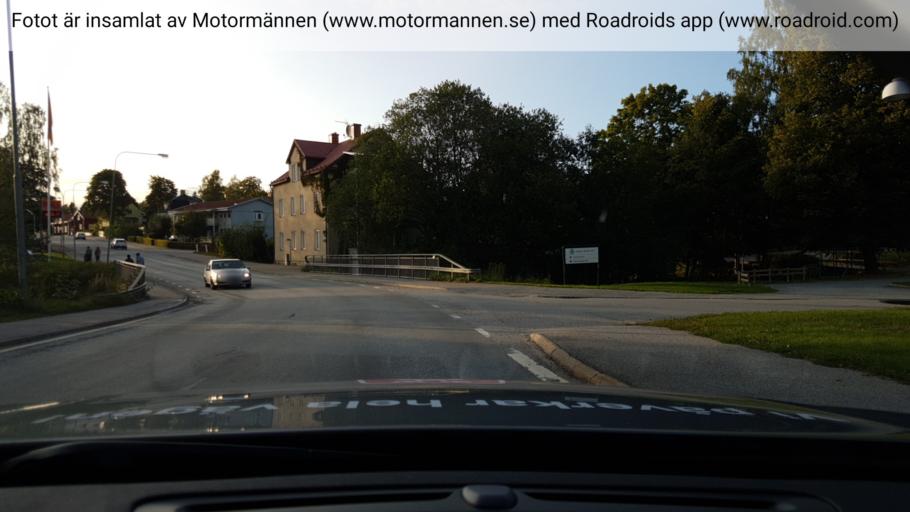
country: SE
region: OErebro
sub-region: Ljusnarsbergs Kommun
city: Kopparberg
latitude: 59.8739
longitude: 15.0020
